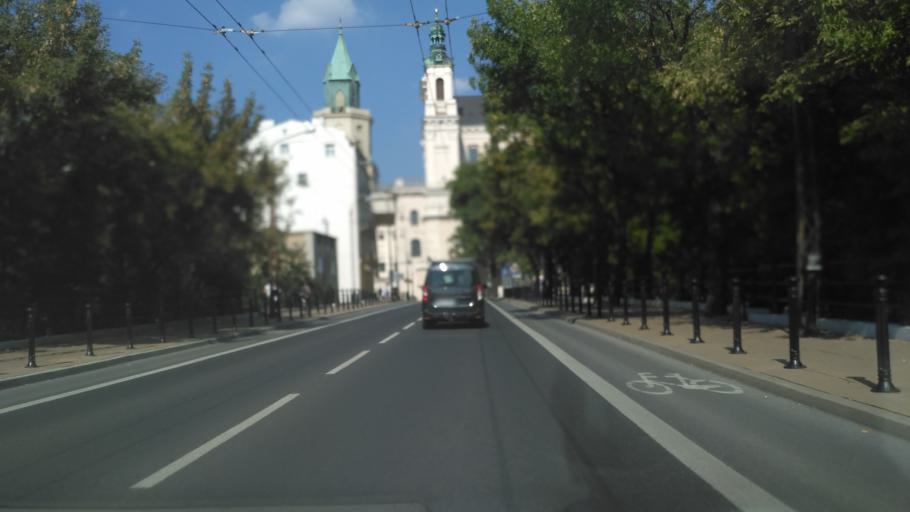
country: PL
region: Lublin Voivodeship
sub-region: Powiat lubelski
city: Lublin
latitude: 51.2454
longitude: 22.5686
